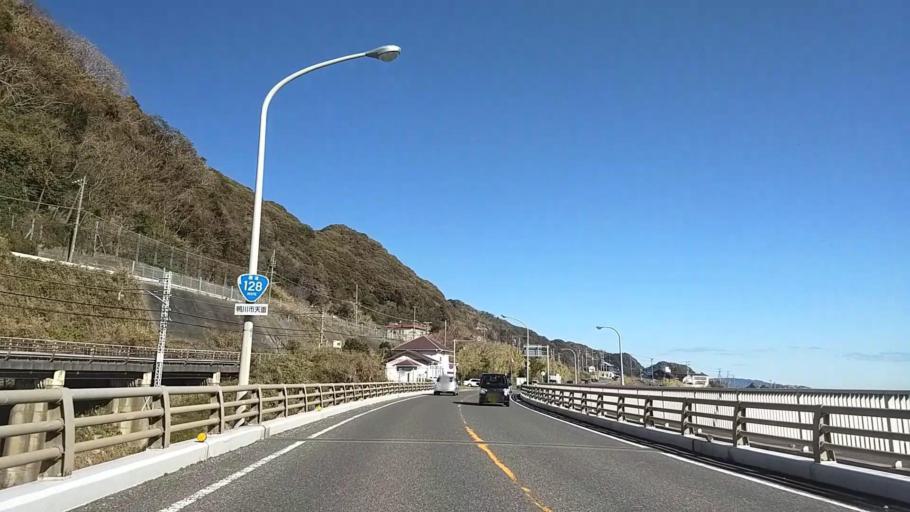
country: JP
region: Chiba
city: Kawaguchi
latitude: 35.0681
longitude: 140.0789
